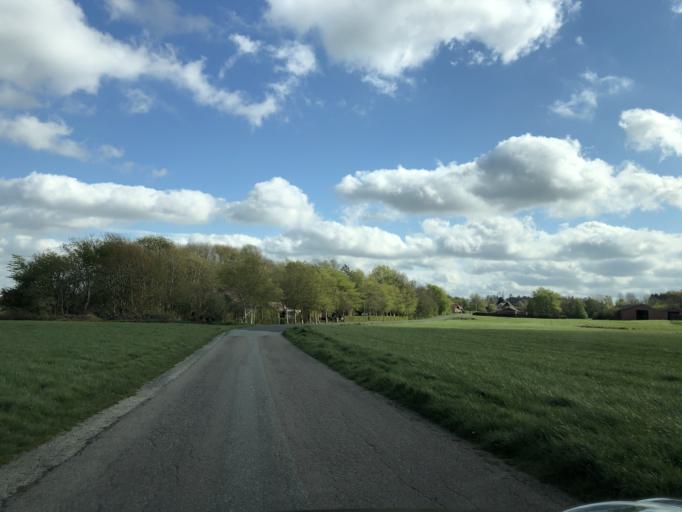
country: DK
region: Central Jutland
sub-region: Holstebro Kommune
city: Holstebro
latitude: 56.2685
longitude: 8.6486
